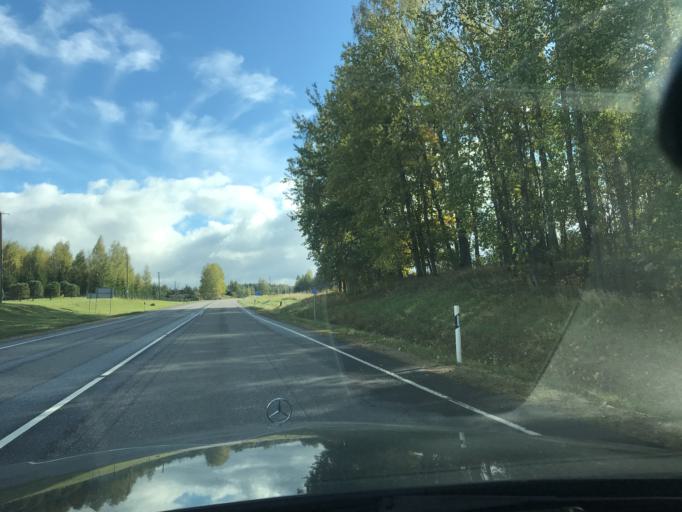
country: EE
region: Vorumaa
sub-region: Voru linn
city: Voru
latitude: 57.8070
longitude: 27.0737
